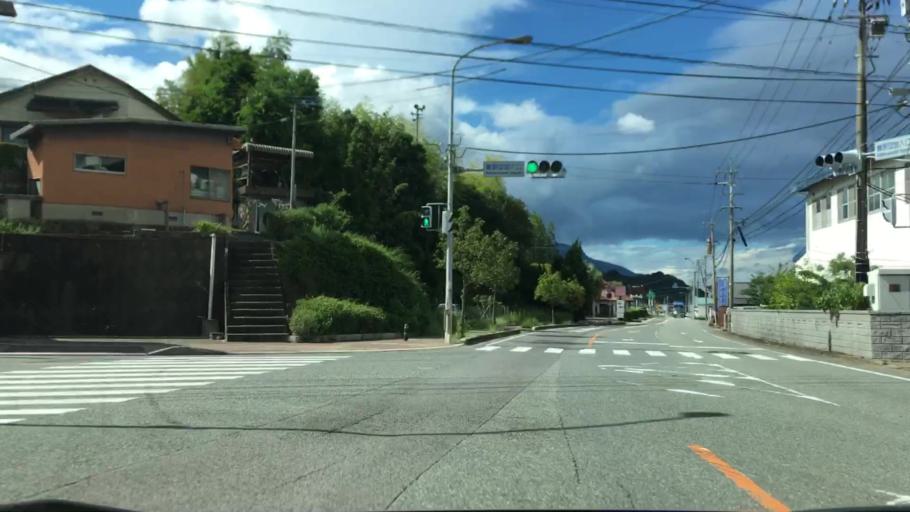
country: JP
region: Saga Prefecture
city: Imaricho-ko
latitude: 33.1878
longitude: 129.8524
